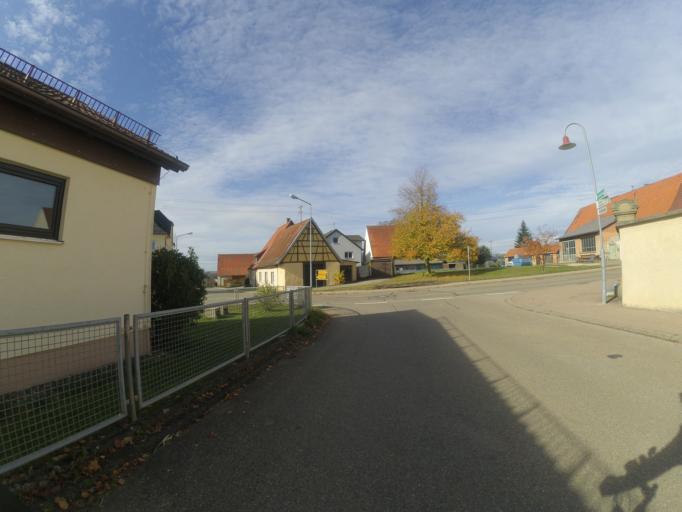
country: DE
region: Baden-Wuerttemberg
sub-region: Tuebingen Region
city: Lonsee
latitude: 48.5820
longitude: 9.9160
